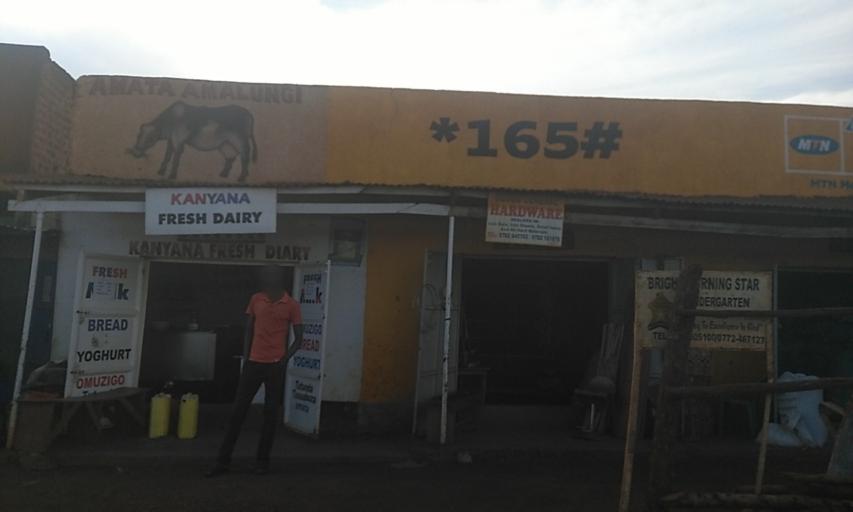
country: UG
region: Central Region
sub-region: Wakiso District
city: Kajansi
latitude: 0.2571
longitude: 32.5075
